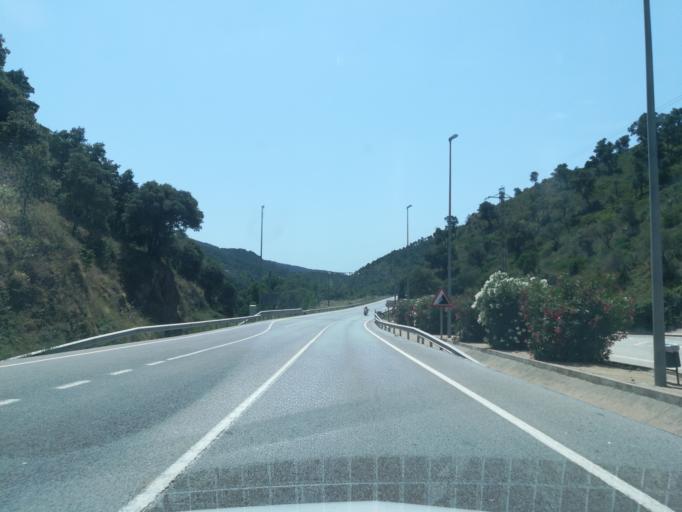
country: ES
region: Catalonia
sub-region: Provincia de Girona
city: la Jonquera
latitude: 42.4570
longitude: 2.8648
